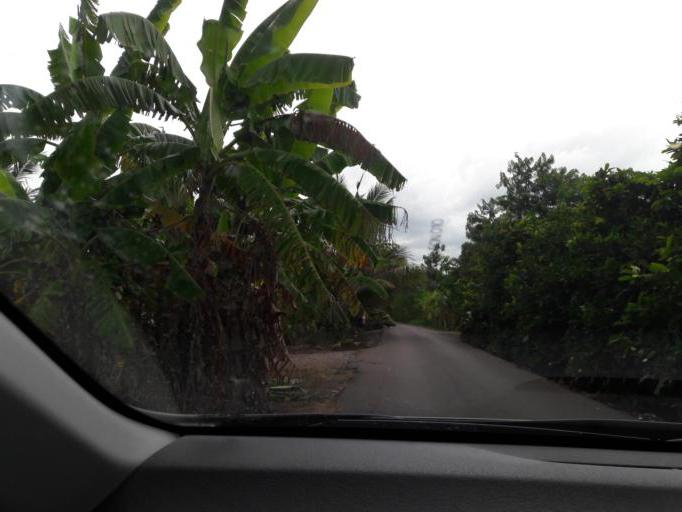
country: TH
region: Ratchaburi
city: Damnoen Saduak
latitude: 13.5444
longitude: 99.9992
